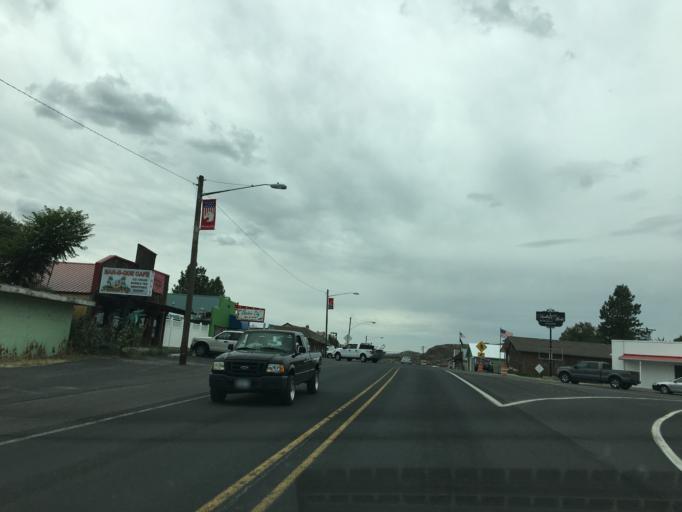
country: US
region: Washington
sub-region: Okanogan County
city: Coulee Dam
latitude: 47.9327
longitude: -119.0379
